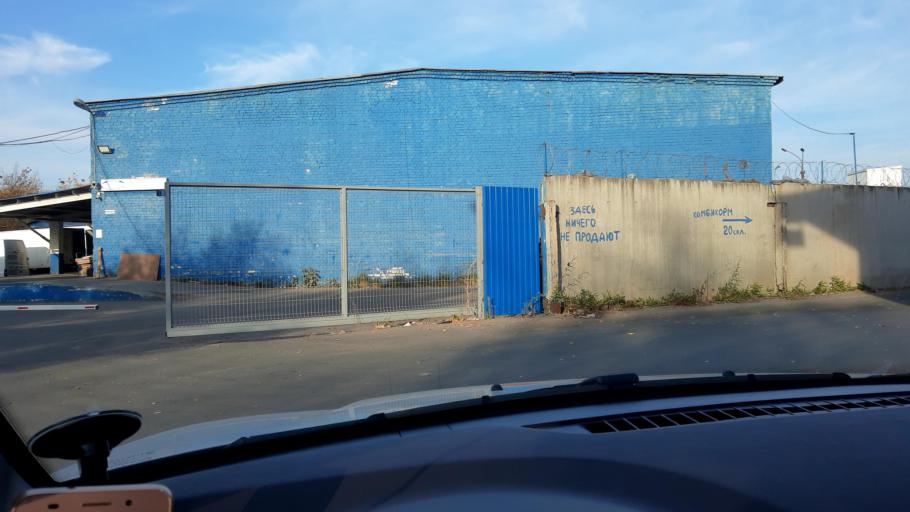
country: RU
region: Nizjnij Novgorod
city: Nizhniy Novgorod
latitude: 56.2601
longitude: 43.9165
